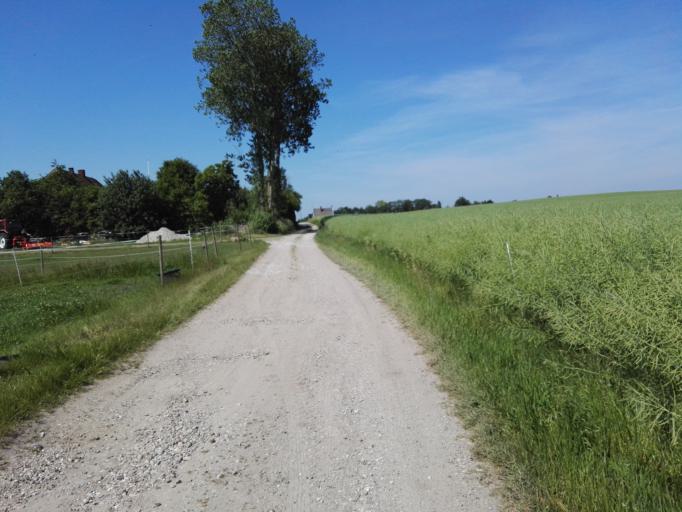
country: DK
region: Capital Region
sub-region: Frederikssund Kommune
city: Jaegerspris
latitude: 55.8049
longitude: 11.9938
